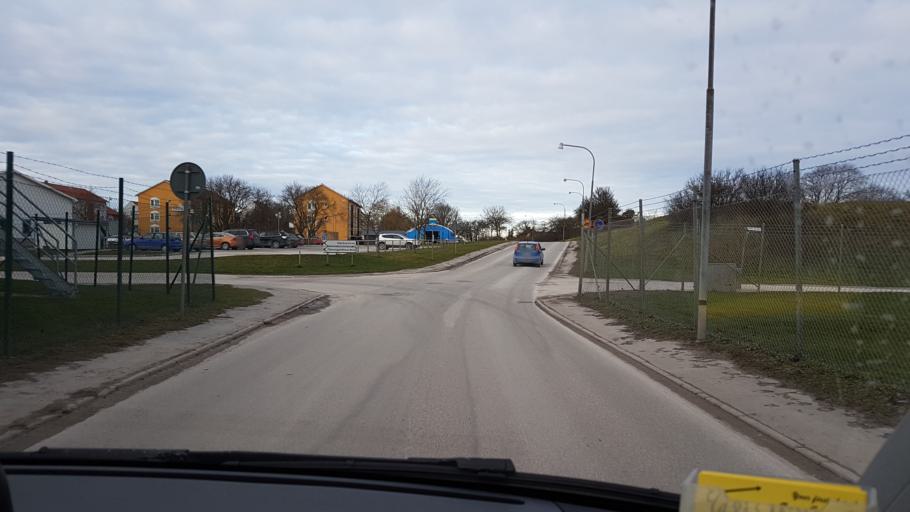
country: SE
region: Gotland
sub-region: Gotland
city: Visby
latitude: 57.6465
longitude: 18.3154
